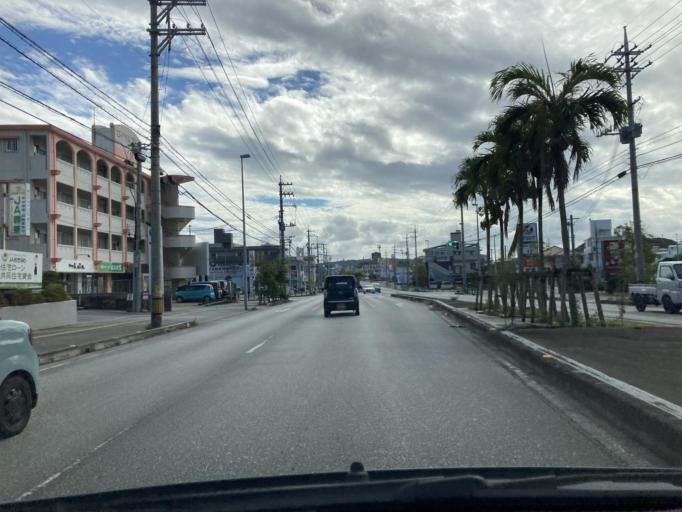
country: JP
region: Okinawa
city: Tomigusuku
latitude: 26.1612
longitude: 127.7229
